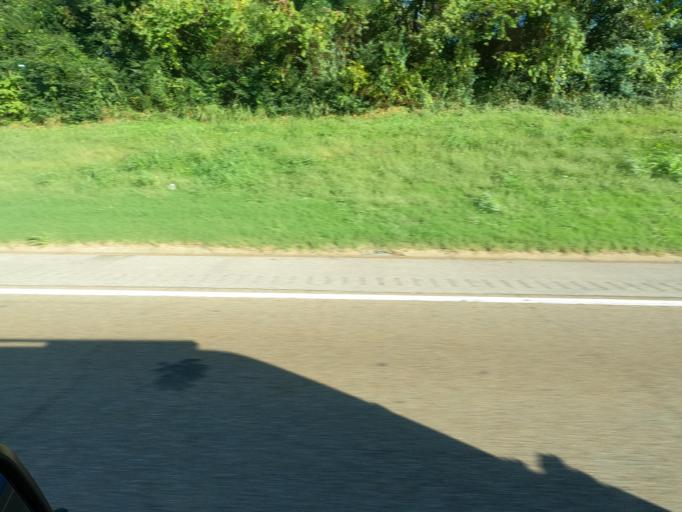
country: US
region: Tennessee
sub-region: Shelby County
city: Memphis
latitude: 35.1161
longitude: -90.0274
